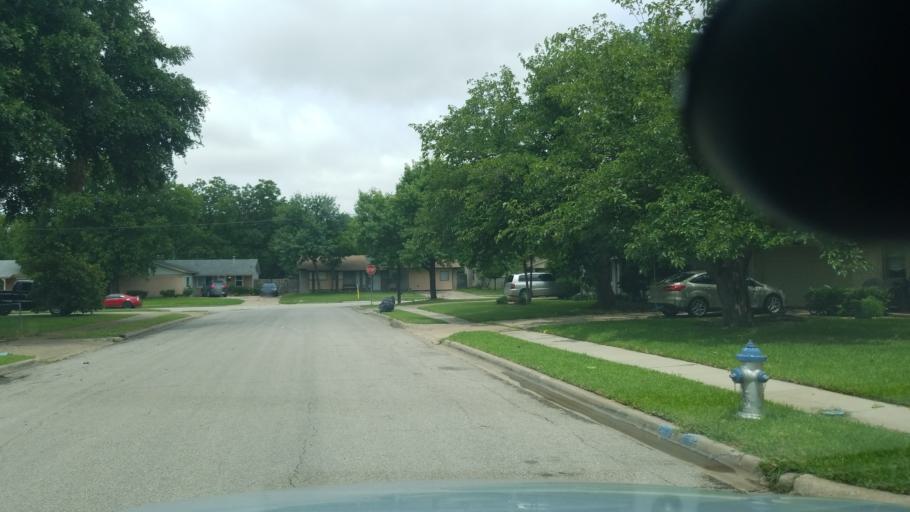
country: US
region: Texas
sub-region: Dallas County
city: Irving
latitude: 32.8431
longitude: -96.9622
